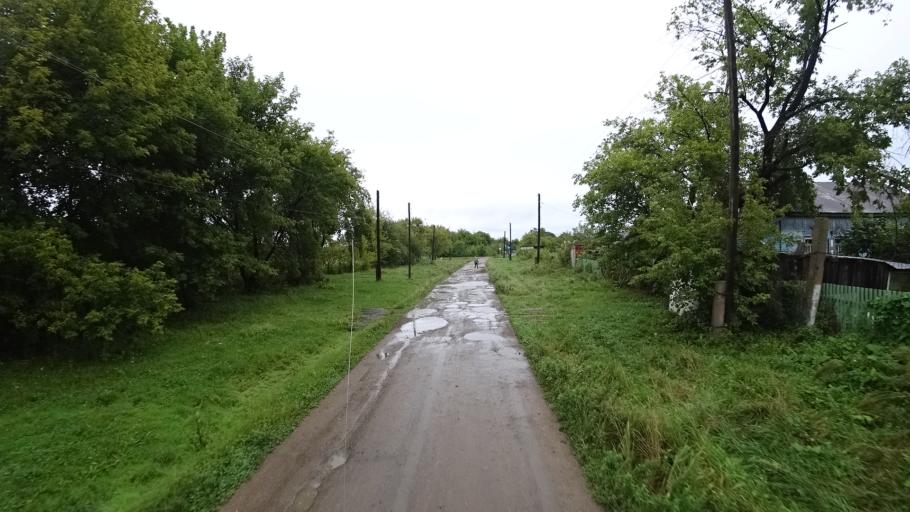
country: RU
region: Primorskiy
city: Monastyrishche
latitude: 44.2554
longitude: 132.4245
